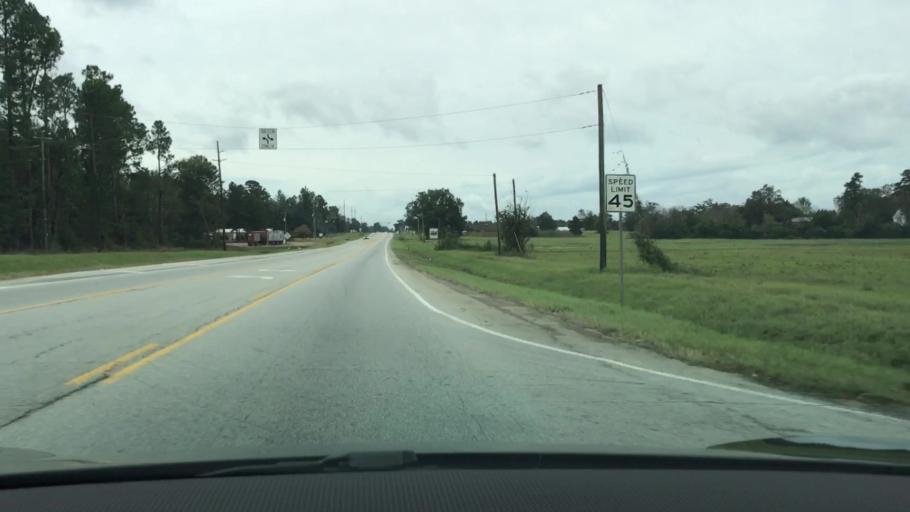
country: US
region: Georgia
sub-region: Jefferson County
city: Louisville
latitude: 33.0281
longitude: -82.4047
